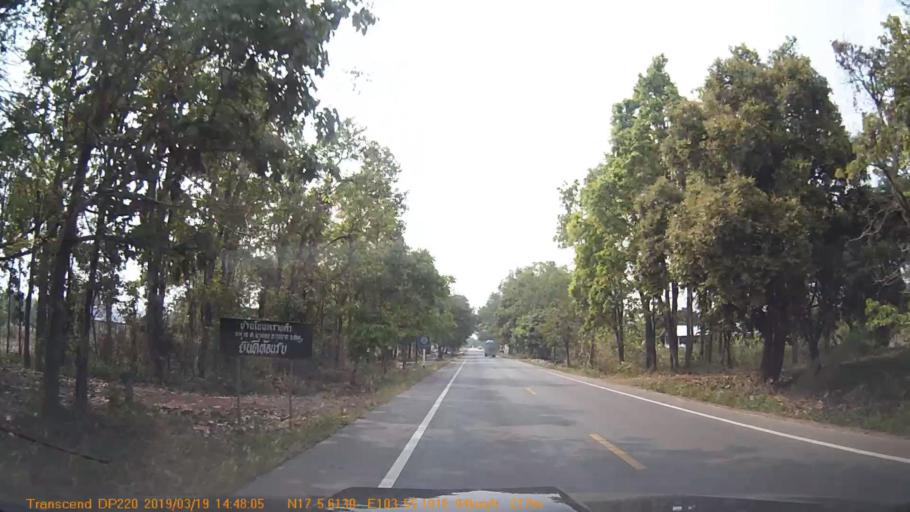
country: TH
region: Sakon Nakhon
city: Kut Bak
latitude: 17.0937
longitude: 103.9182
